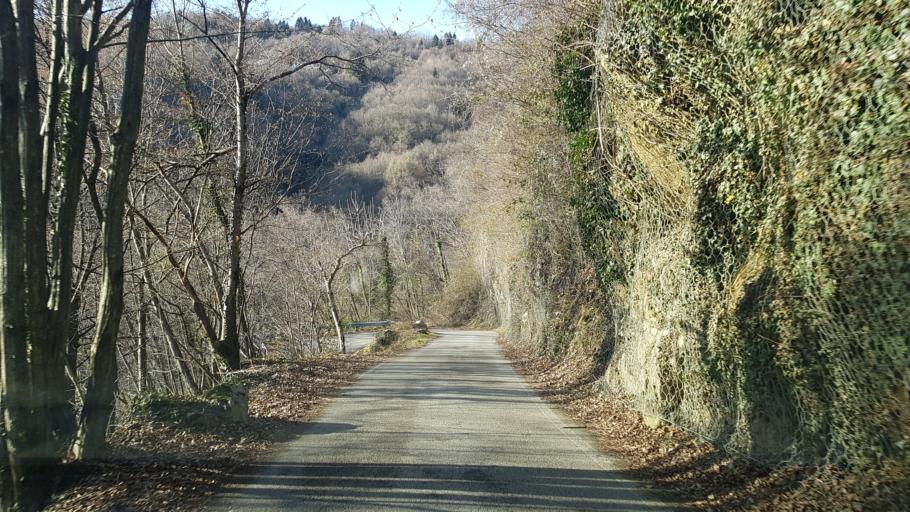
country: IT
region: Friuli Venezia Giulia
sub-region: Provincia di Udine
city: Clodig
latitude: 46.1611
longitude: 13.5821
